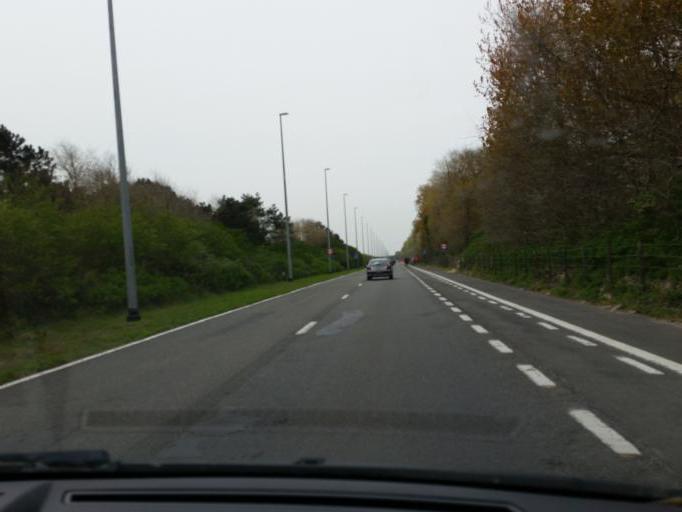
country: BE
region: Flanders
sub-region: Provincie West-Vlaanderen
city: Wenduine
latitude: 51.2909
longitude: 3.0603
